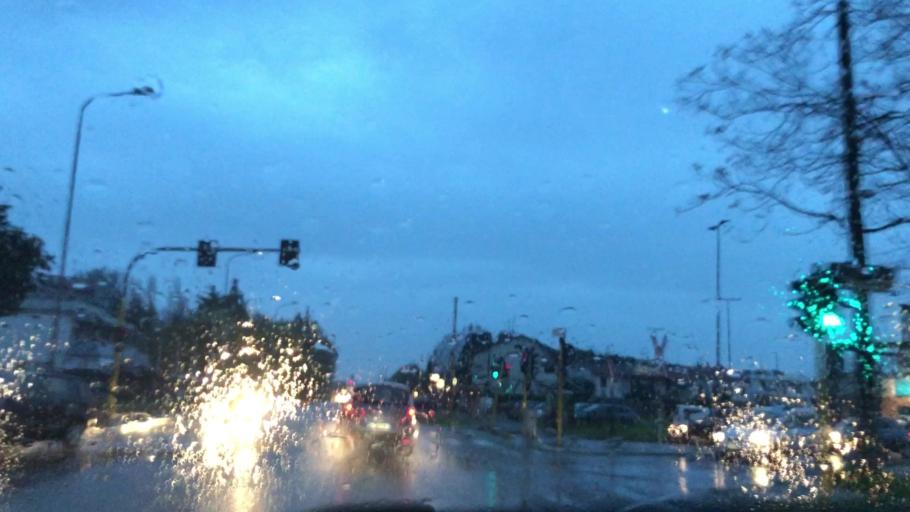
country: IT
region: Lombardy
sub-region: Citta metropolitana di Milano
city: Cusano Milanino
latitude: 45.5688
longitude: 9.1902
